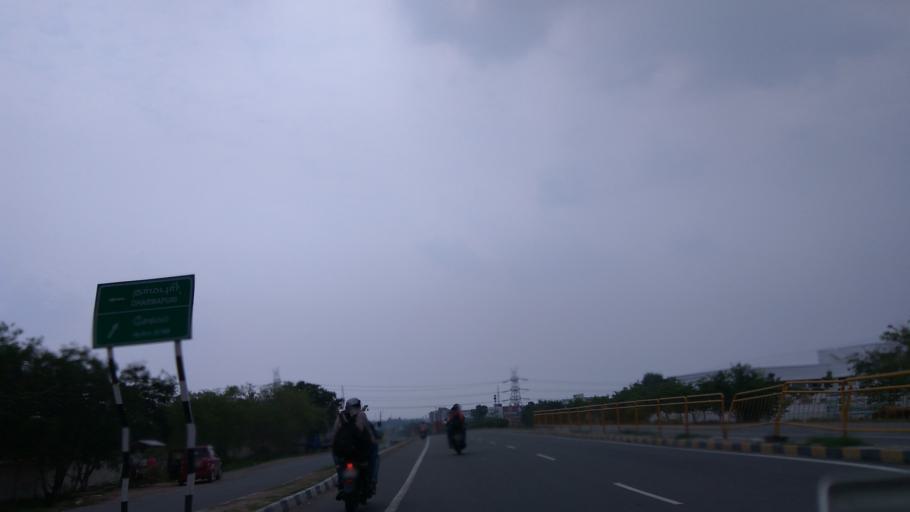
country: IN
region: Tamil Nadu
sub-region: Dharmapuri
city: Dharmapuri
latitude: 12.1789
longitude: 78.1723
